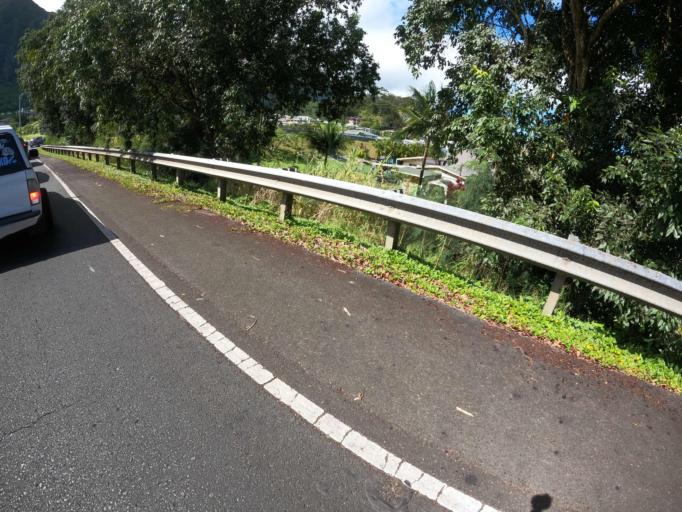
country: US
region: Hawaii
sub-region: Honolulu County
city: Kane'ohe
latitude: 21.4035
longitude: -157.8062
